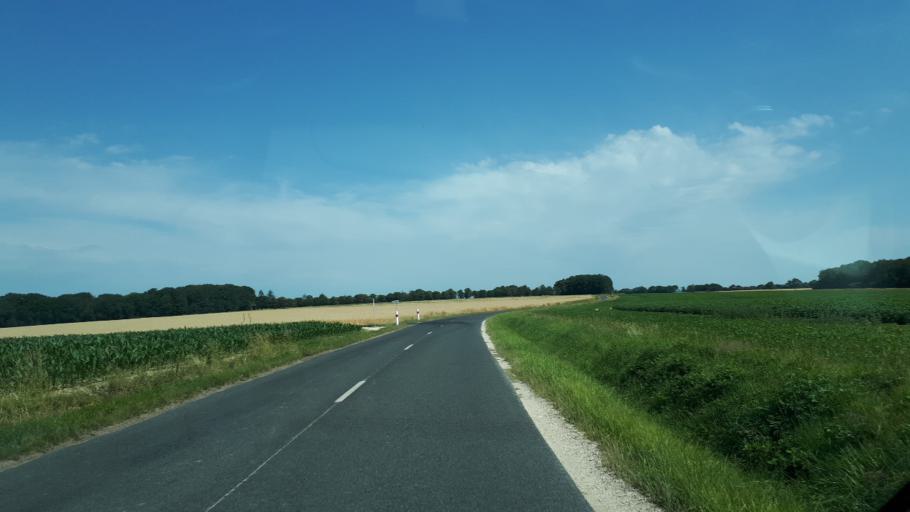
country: FR
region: Centre
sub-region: Departement du Loir-et-Cher
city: La Ville-aux-Clercs
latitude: 47.9436
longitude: 1.0807
